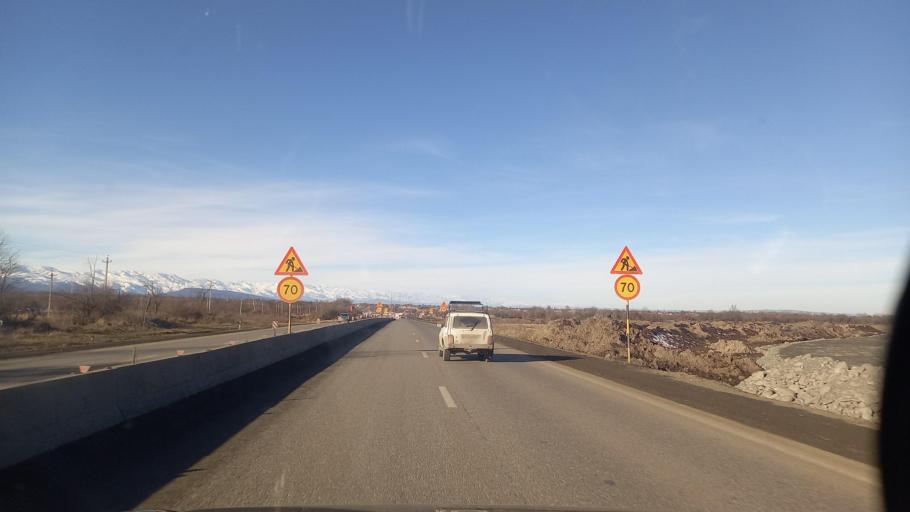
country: RU
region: North Ossetia
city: Gizel'
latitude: 43.0271
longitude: 44.6113
